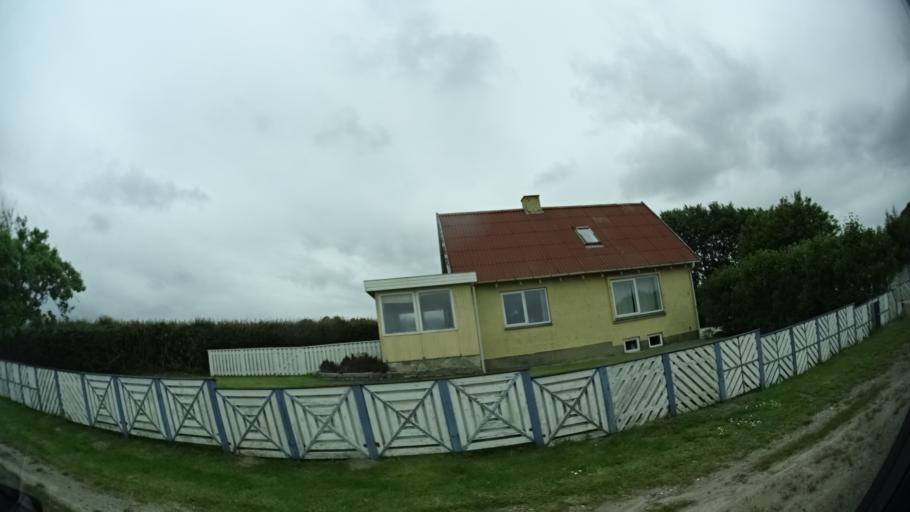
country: DK
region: Central Jutland
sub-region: Syddjurs Kommune
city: Hornslet
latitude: 56.2966
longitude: 10.3543
